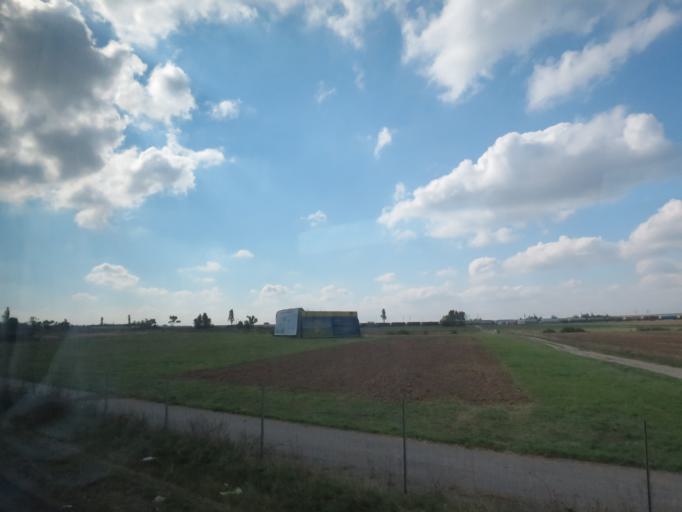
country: AT
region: Lower Austria
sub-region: Politischer Bezirk Wien-Umgebung
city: Rauchenwarth
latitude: 48.1380
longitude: 16.5255
